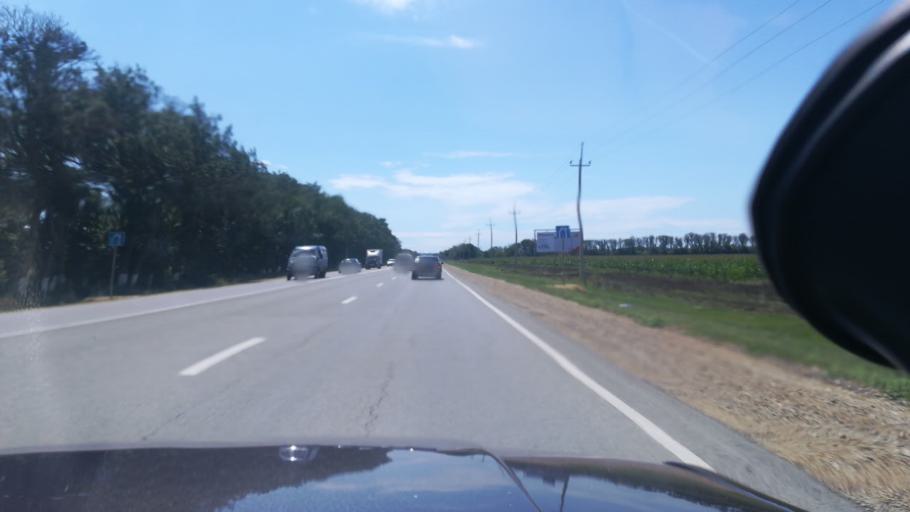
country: RU
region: Krasnodarskiy
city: Tsibanobalka
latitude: 44.9979
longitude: 37.3212
